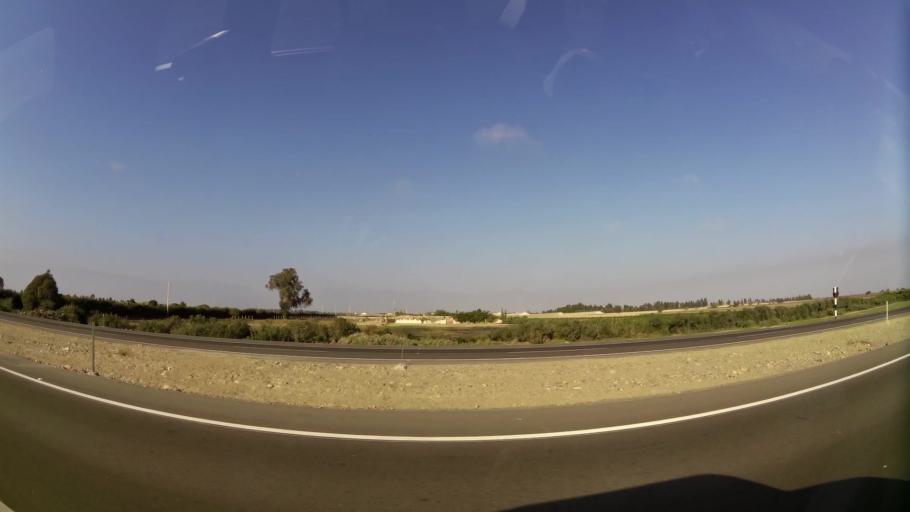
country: PE
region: Ica
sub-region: Provincia de Chincha
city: Chincha Baja
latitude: -13.4941
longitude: -76.1851
